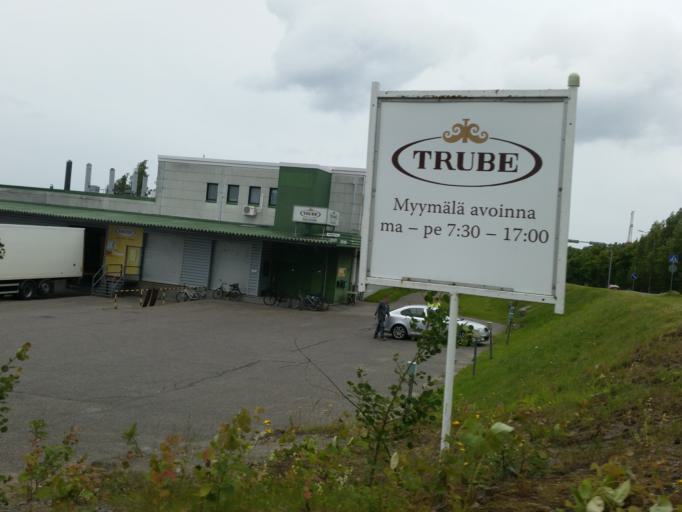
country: FI
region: Northern Savo
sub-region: Kuopio
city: Kuopio
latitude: 62.8978
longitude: 27.7083
